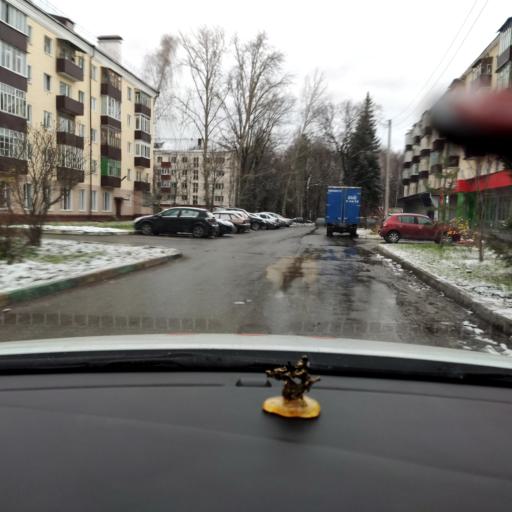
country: RU
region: Tatarstan
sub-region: Zelenodol'skiy Rayon
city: Zelenodolsk
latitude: 55.8448
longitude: 48.5073
